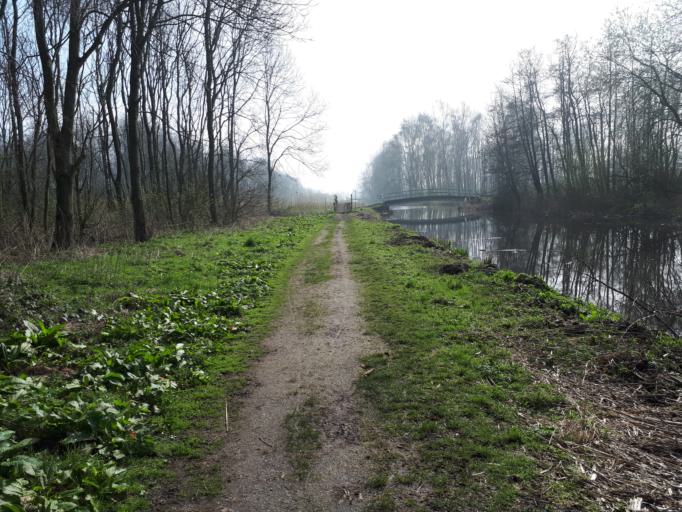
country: NL
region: South Holland
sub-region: Gemeente Krimpen aan den IJssel
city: Krimpen aan den IJssel
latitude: 51.9426
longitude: 4.6132
